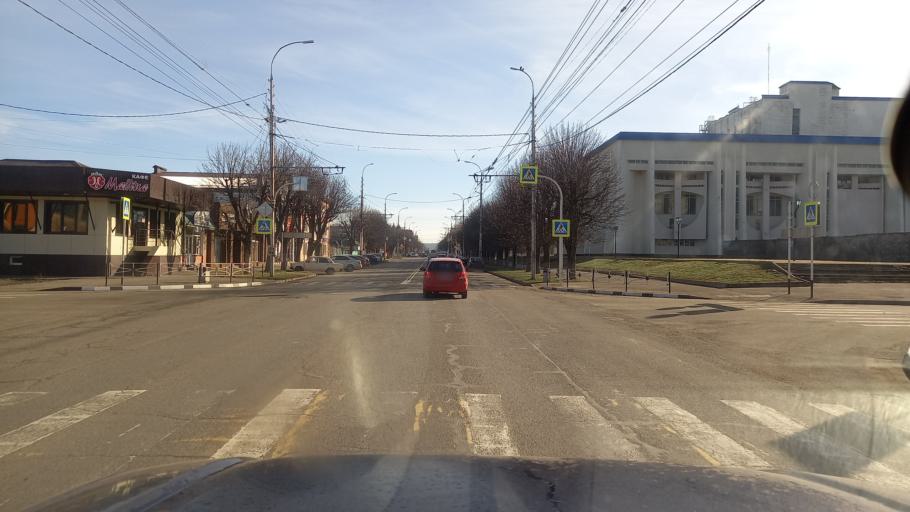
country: RU
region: Adygeya
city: Maykop
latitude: 44.6100
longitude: 40.0979
